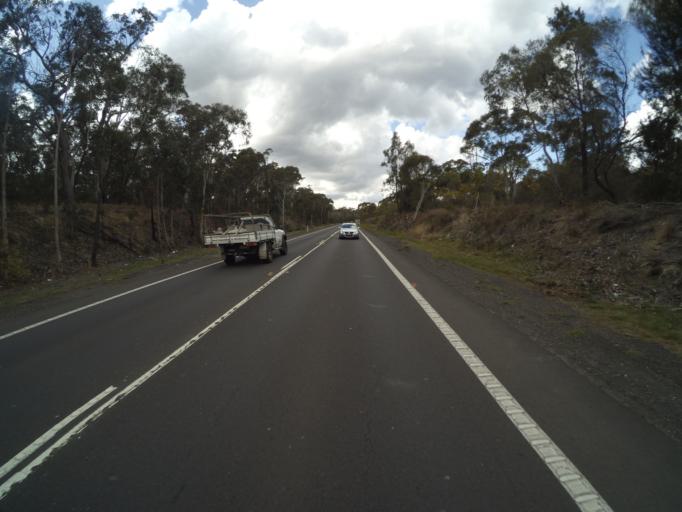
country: AU
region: New South Wales
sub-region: Wollondilly
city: Douglas Park
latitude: -34.2907
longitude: 150.7294
